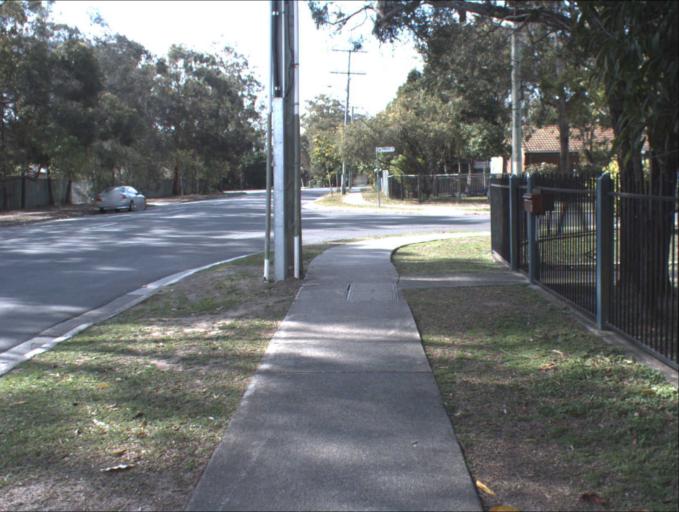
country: AU
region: Queensland
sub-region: Logan
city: Waterford West
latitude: -27.6712
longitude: 153.1319
